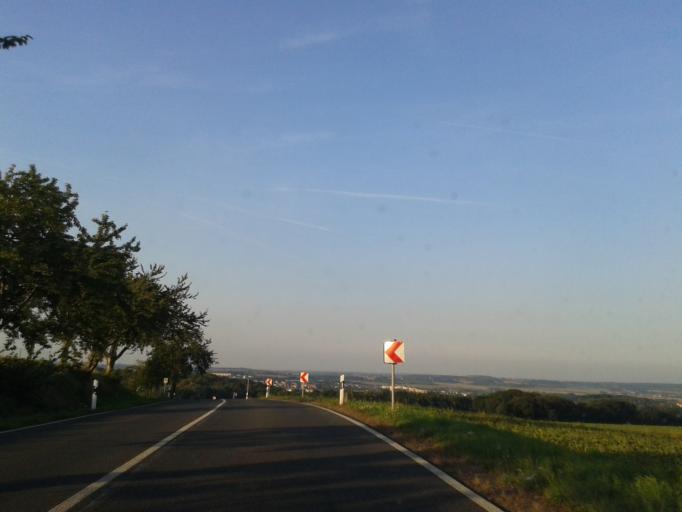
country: DE
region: Saxony
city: Meissen
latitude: 51.1419
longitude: 13.4746
